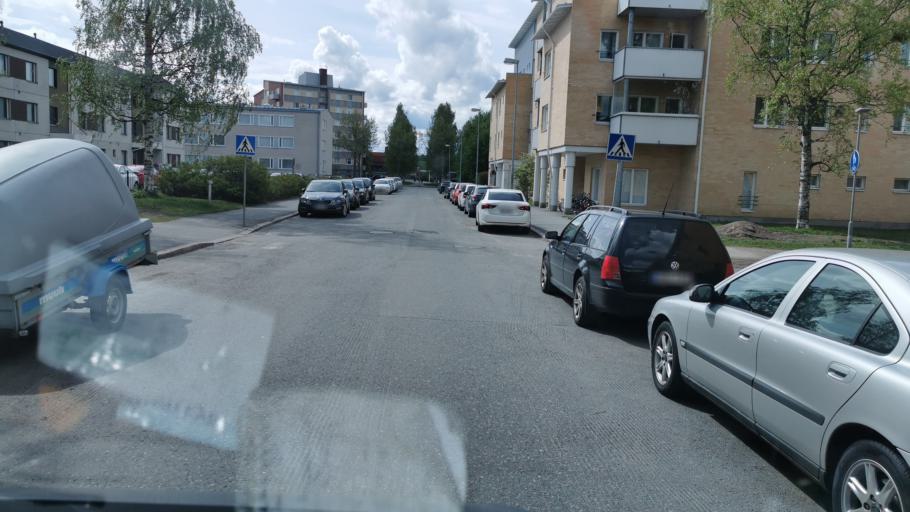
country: FI
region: Northern Ostrobothnia
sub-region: Oulu
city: Oulu
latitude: 65.0042
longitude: 25.4589
